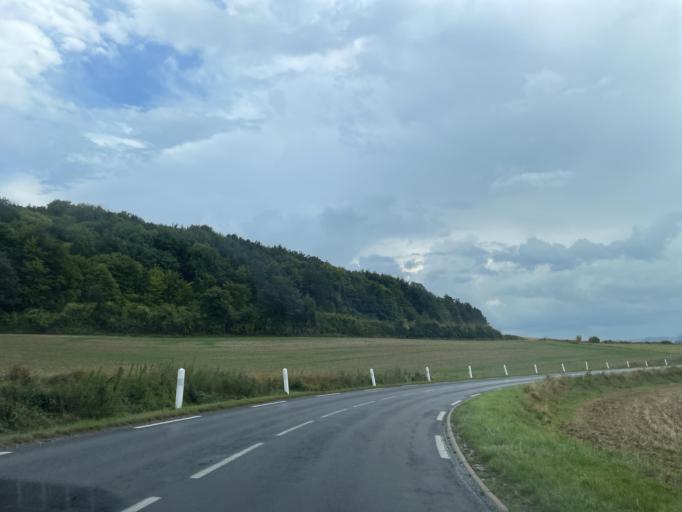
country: FR
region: Haute-Normandie
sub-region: Departement de la Seine-Maritime
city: Neufchatel-en-Bray
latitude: 49.7496
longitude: 1.4339
